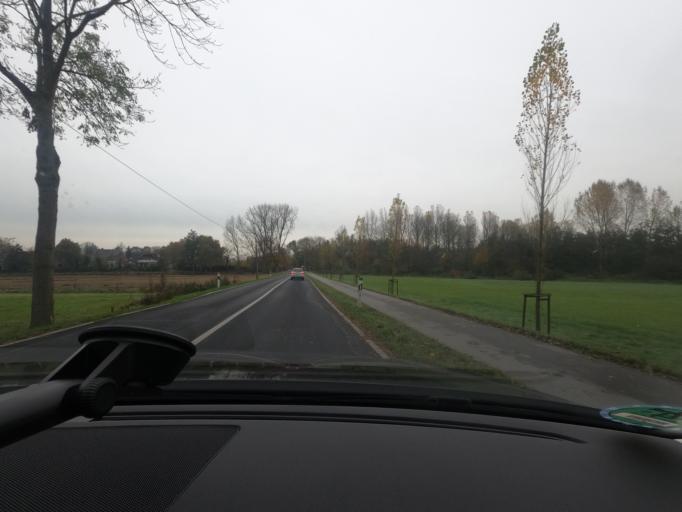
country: DE
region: North Rhine-Westphalia
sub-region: Regierungsbezirk Dusseldorf
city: Kevelaer
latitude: 51.5940
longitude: 6.2913
